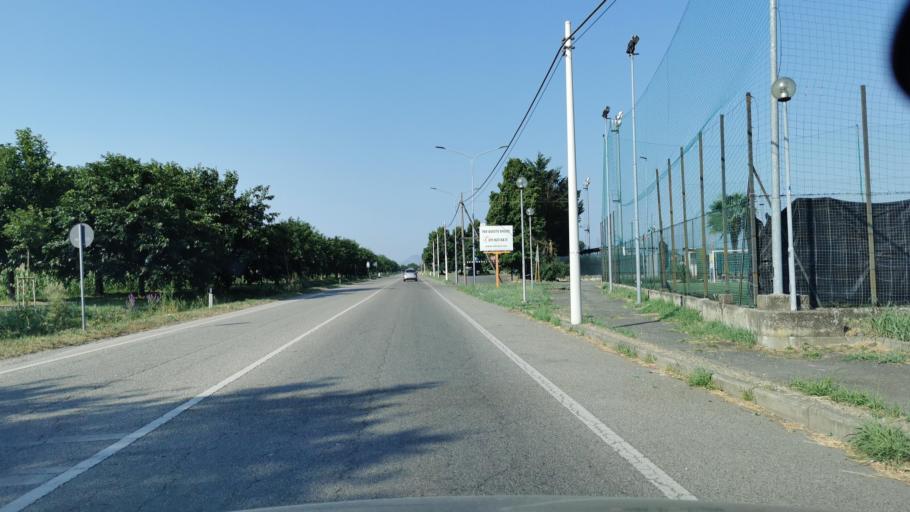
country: IT
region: Piedmont
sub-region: Provincia di Torino
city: Savonera
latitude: 45.1171
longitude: 7.6095
